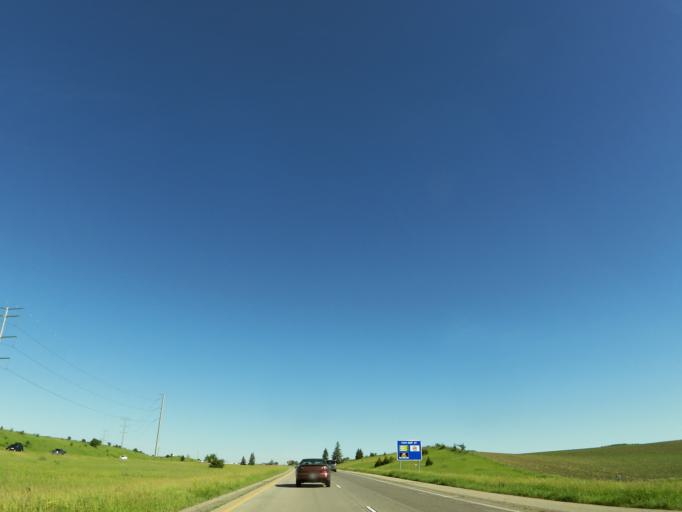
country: US
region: Minnesota
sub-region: Otter Tail County
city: Fergus Falls
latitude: 46.2387
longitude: -96.0563
